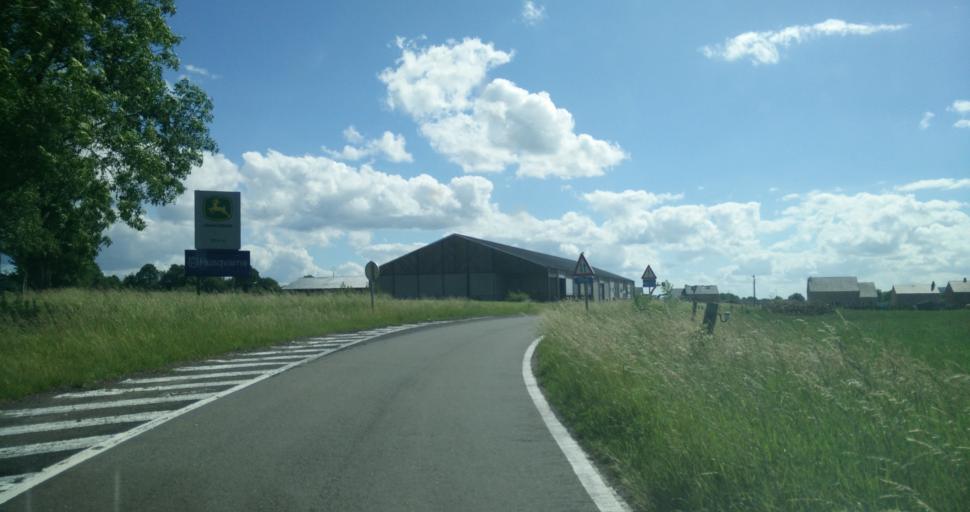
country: BE
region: Wallonia
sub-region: Province du Luxembourg
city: Marche-en-Famenne
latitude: 50.1882
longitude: 5.3705
